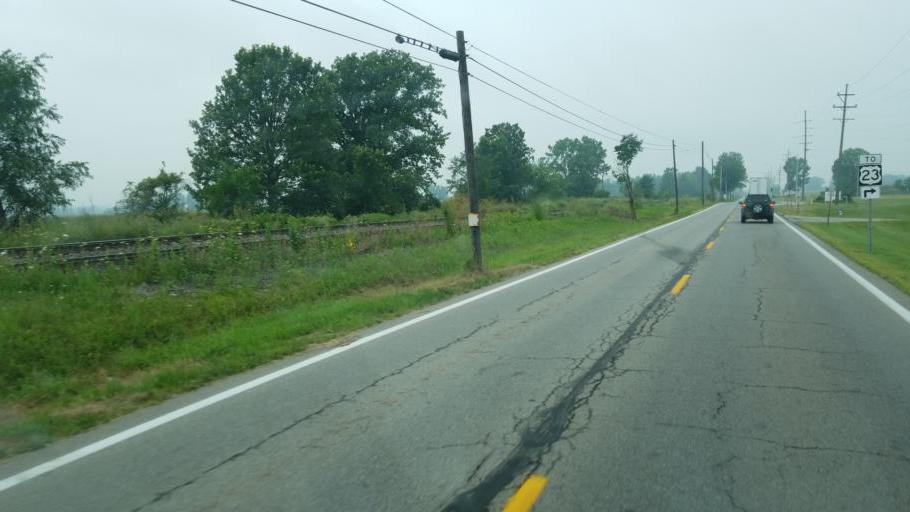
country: US
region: Ohio
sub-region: Marion County
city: Marion
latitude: 40.5860
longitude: -83.1744
